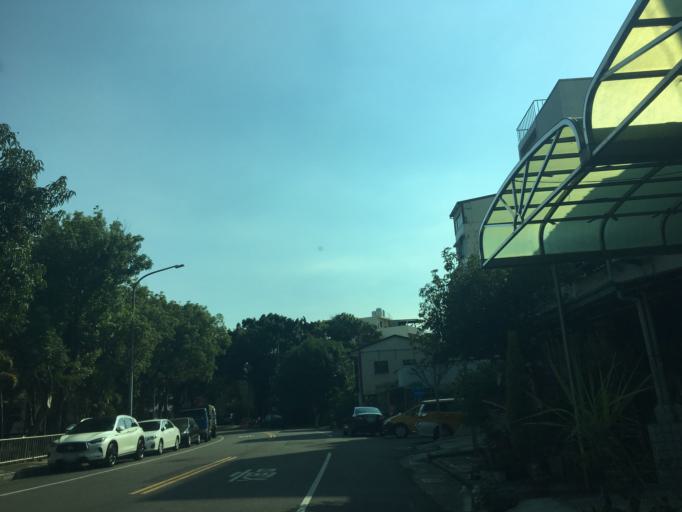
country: TW
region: Taiwan
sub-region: Taichung City
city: Taichung
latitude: 24.1551
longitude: 120.6292
